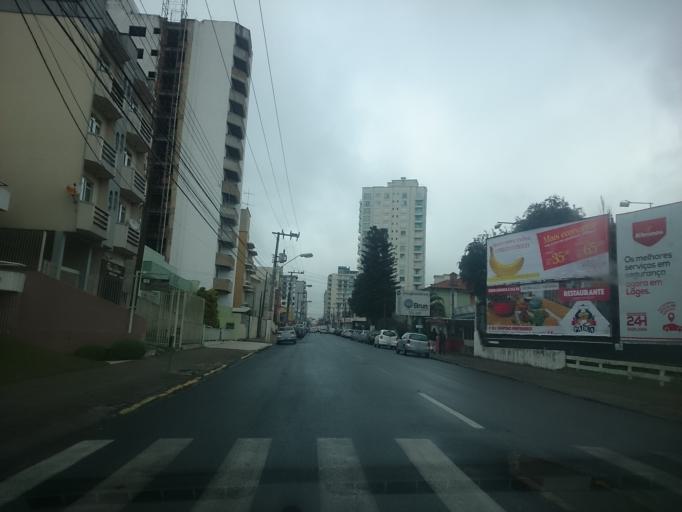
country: BR
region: Santa Catarina
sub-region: Lages
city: Lages
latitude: -27.8111
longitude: -50.3234
